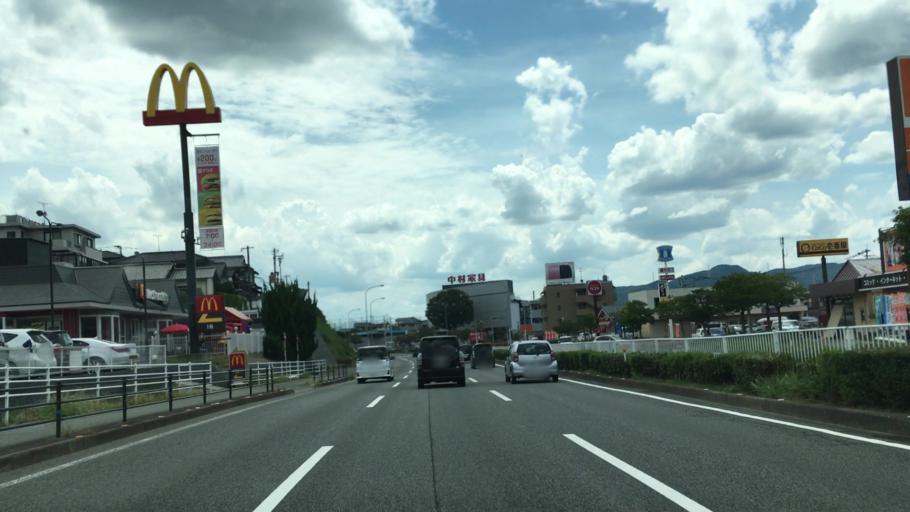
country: JP
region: Fukuoka
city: Dazaifu
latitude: 33.5016
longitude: 130.5314
